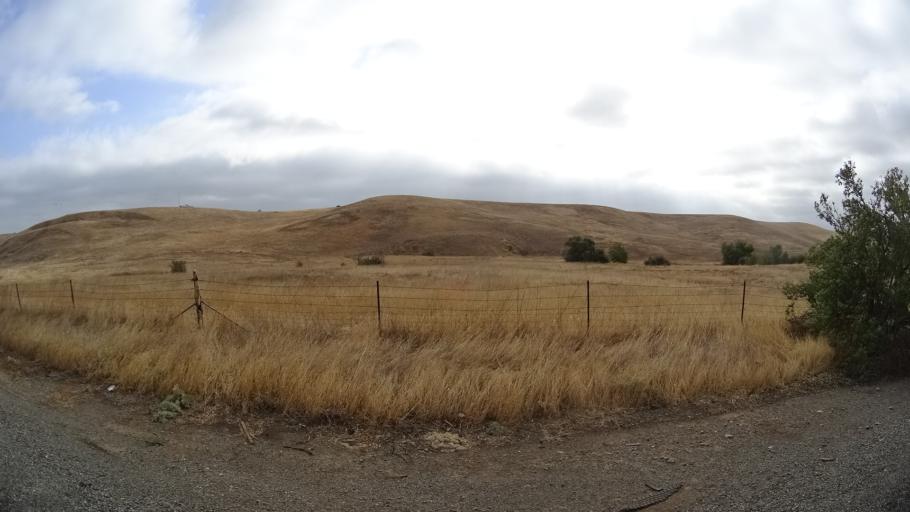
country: US
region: California
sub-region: Yolo County
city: Dunnigan
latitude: 38.7920
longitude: -121.9142
